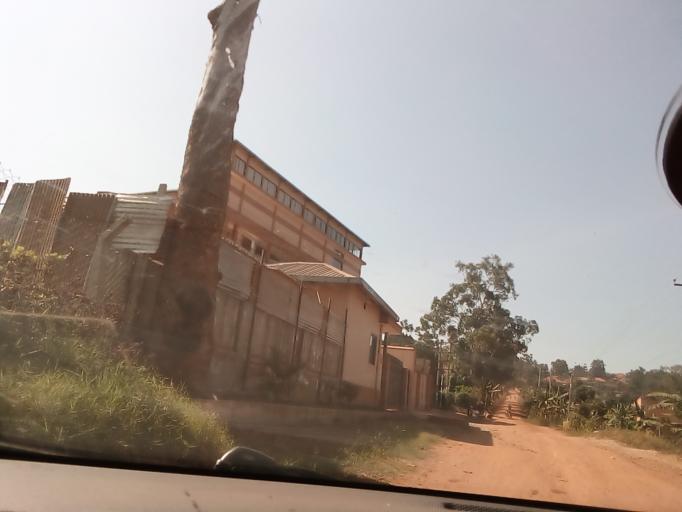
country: UG
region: Central Region
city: Masaka
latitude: -0.3291
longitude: 31.7324
